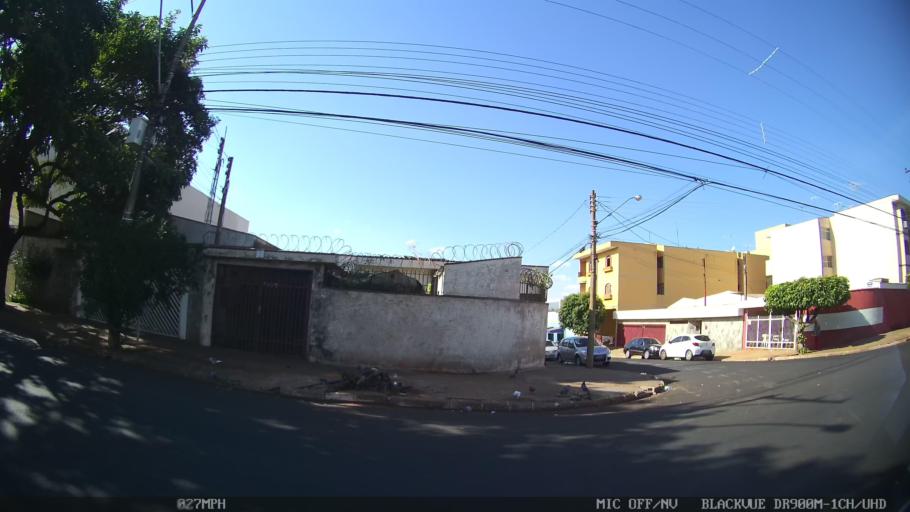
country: BR
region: Sao Paulo
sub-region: Ribeirao Preto
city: Ribeirao Preto
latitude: -21.1871
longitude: -47.7807
